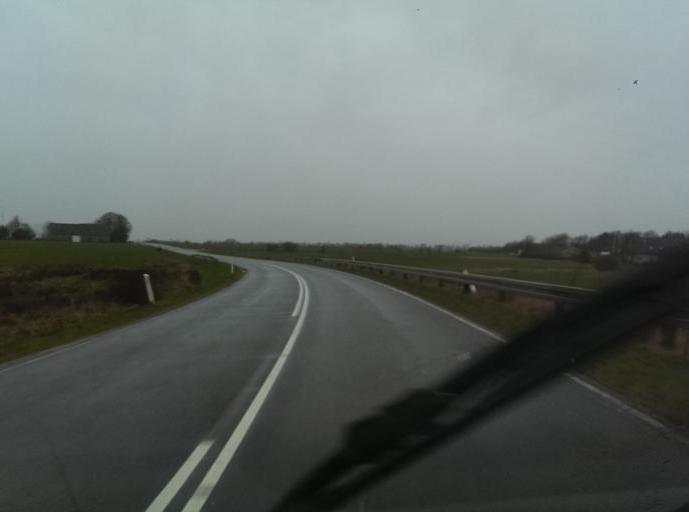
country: DK
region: South Denmark
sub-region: Esbjerg Kommune
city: Tjaereborg
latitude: 55.5030
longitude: 8.5592
